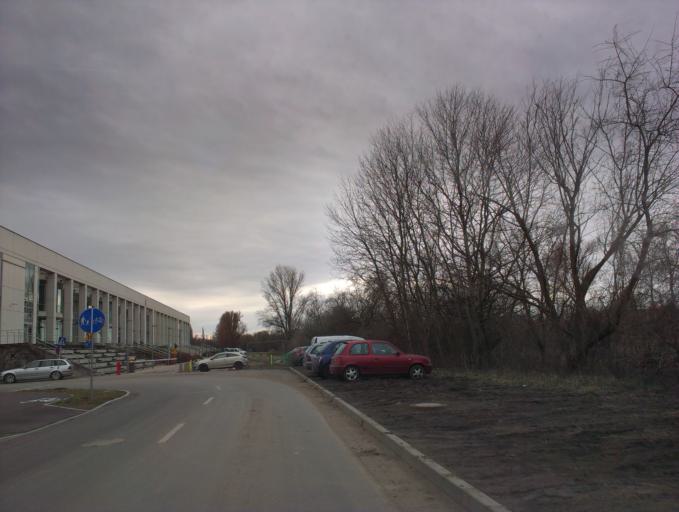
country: PL
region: Greater Poland Voivodeship
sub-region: Poznan
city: Poznan
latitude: 52.4051
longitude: 16.9496
